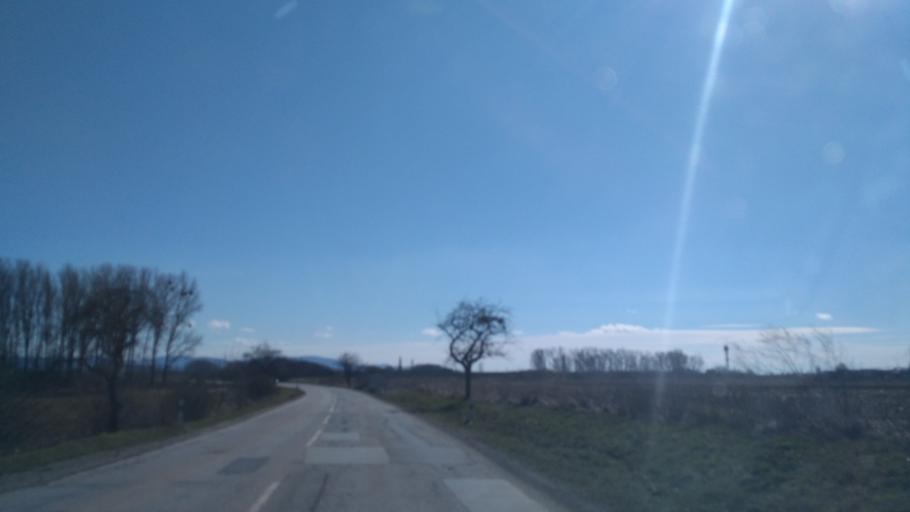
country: SK
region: Kosicky
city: Kosice
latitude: 48.6601
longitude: 21.2767
